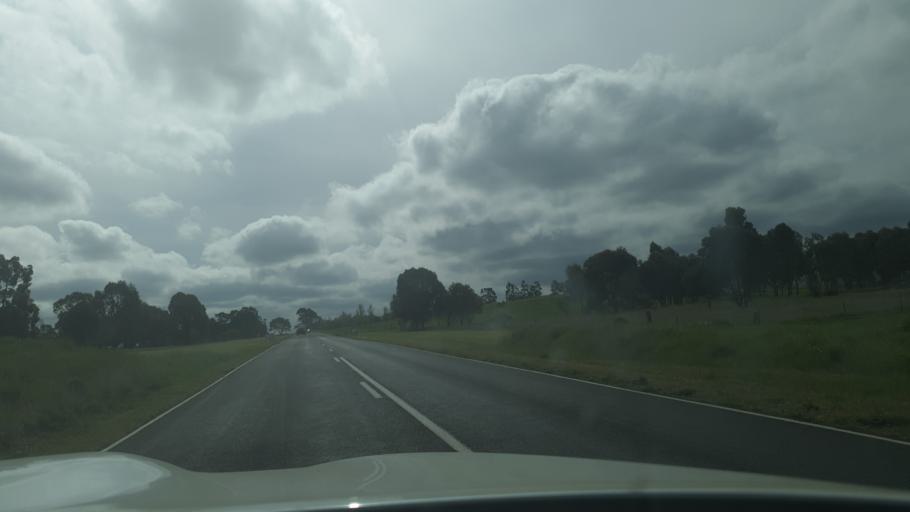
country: AU
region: Victoria
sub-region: Central Goldfields
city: Maryborough
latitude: -37.2108
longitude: 143.7220
